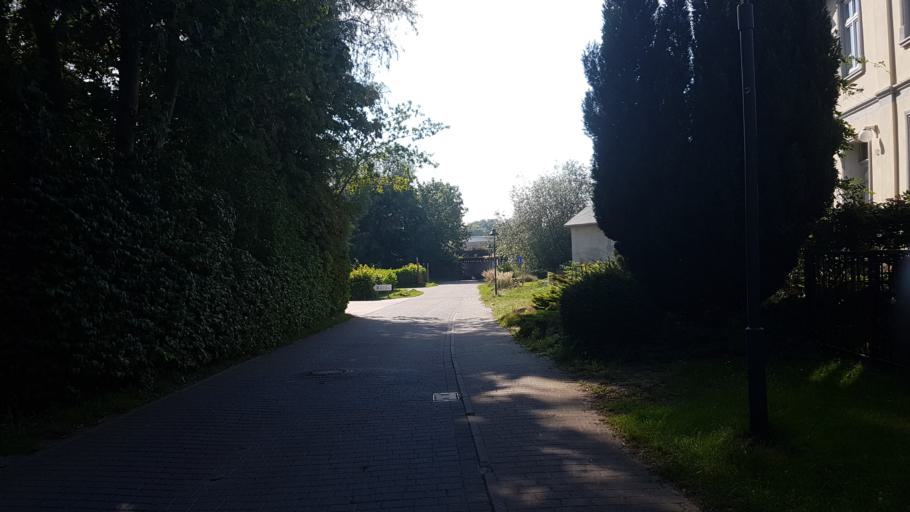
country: DE
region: Mecklenburg-Vorpommern
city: Putbus
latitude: 54.3442
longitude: 13.5029
